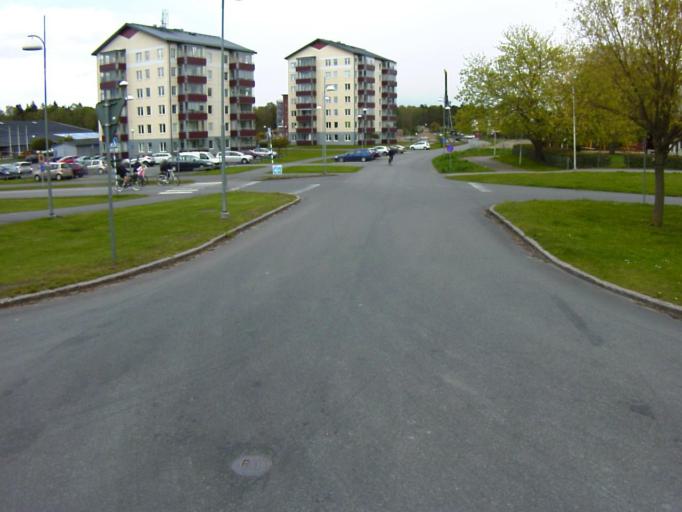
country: SE
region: Skane
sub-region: Kristianstads Kommun
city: Kristianstad
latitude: 56.0439
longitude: 14.1653
